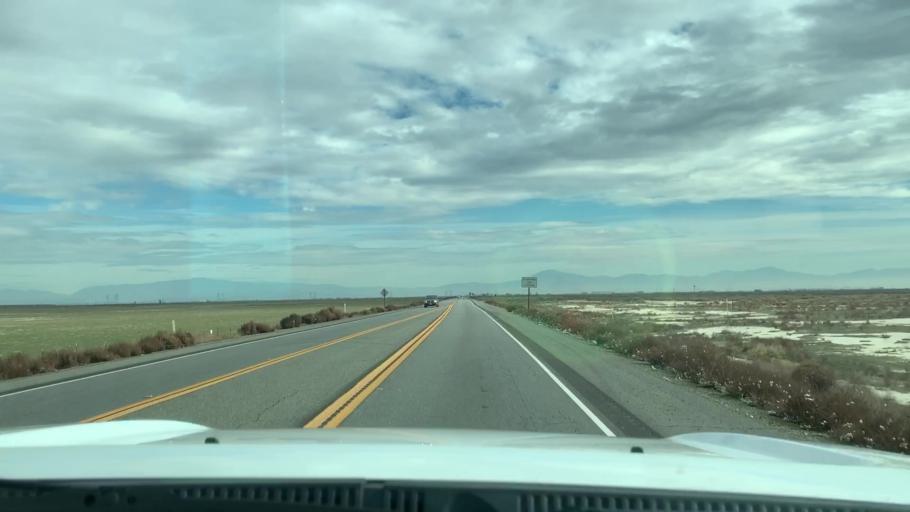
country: US
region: California
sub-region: Kern County
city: Rosedale
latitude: 35.2675
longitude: -119.2871
